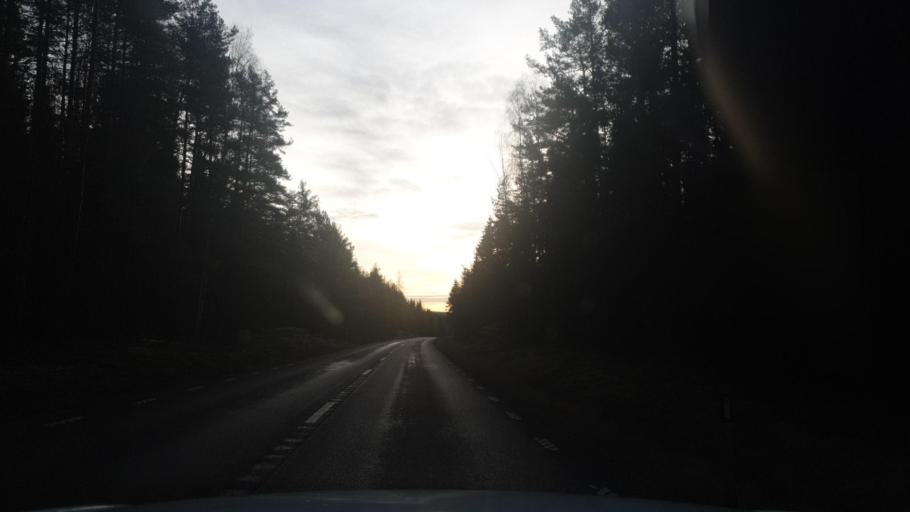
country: SE
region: Vaermland
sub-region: Arvika Kommun
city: Arvika
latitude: 59.5386
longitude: 12.7549
